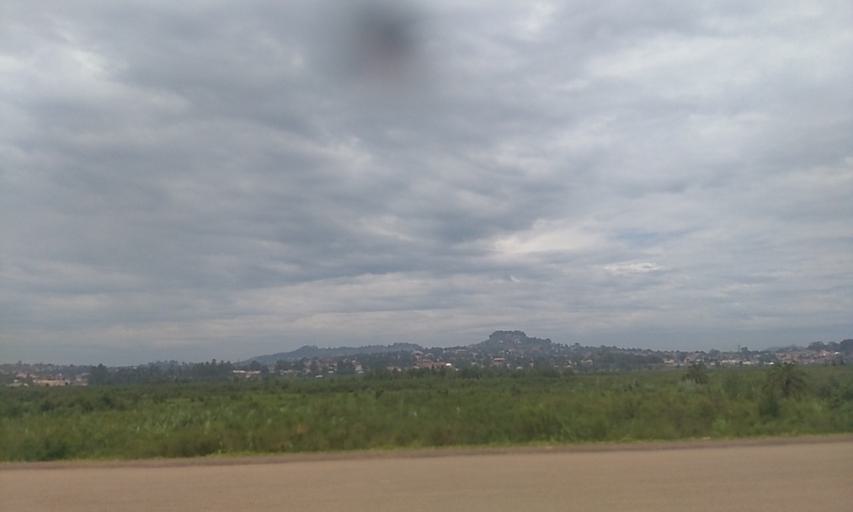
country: UG
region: Central Region
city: Kampala Central Division
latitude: 0.3164
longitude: 32.5199
